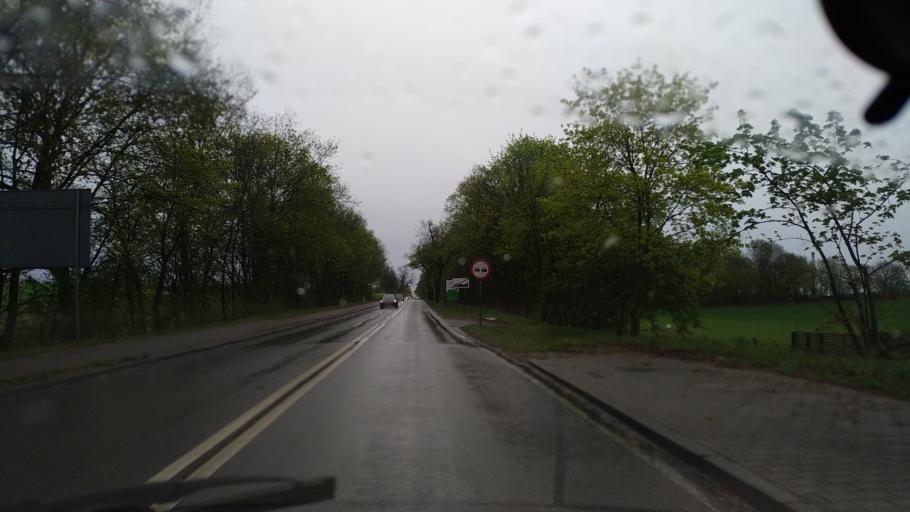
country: PL
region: Greater Poland Voivodeship
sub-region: Powiat zlotowski
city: Zlotow
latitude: 53.3489
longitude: 17.0290
